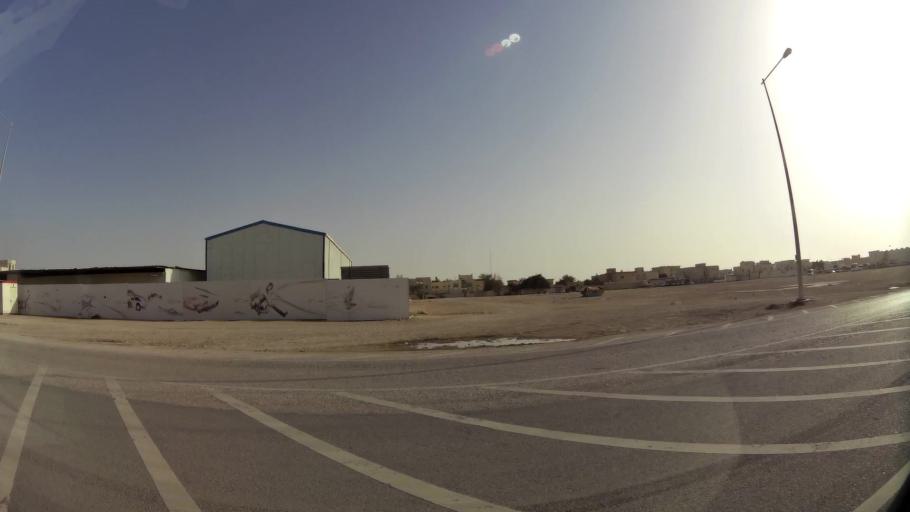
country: QA
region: Baladiyat ar Rayyan
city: Ar Rayyan
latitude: 25.3322
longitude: 51.4306
